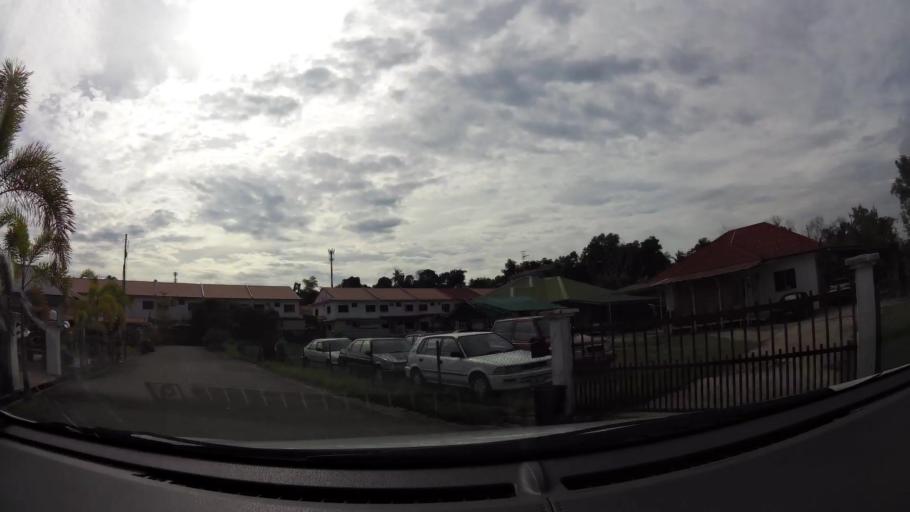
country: BN
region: Brunei and Muara
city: Bandar Seri Begawan
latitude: 4.8973
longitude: 114.8920
